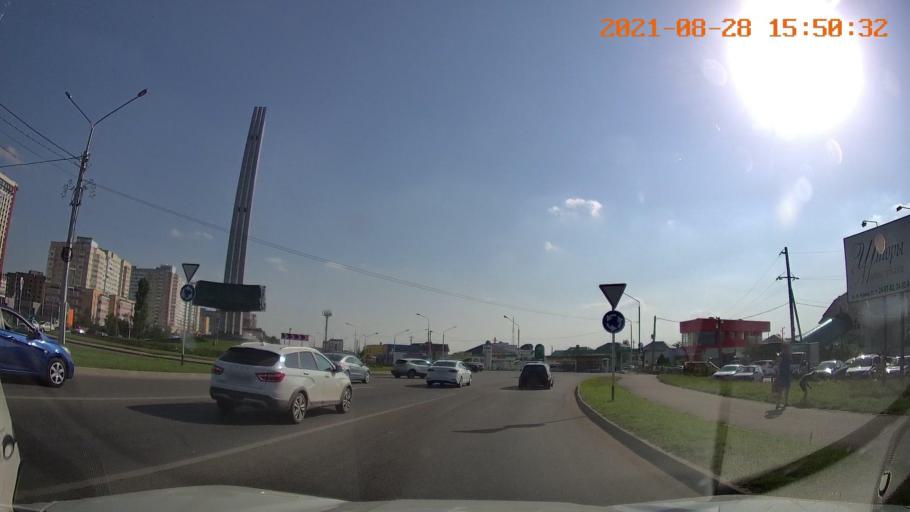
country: RU
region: Stavropol'skiy
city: Tatarka
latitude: 44.9894
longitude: 41.9219
